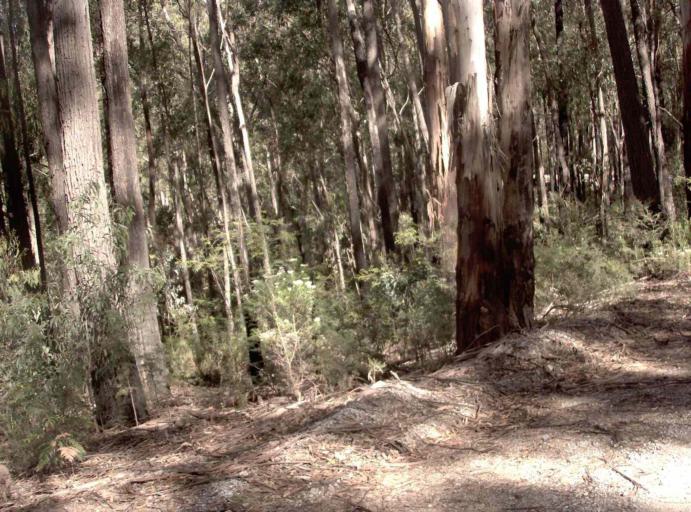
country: AU
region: Victoria
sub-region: East Gippsland
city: Lakes Entrance
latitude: -37.3921
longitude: 148.1228
